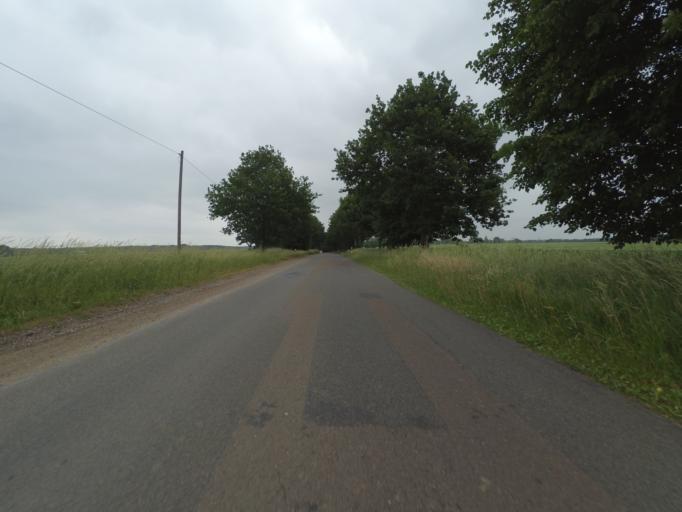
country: DE
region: Mecklenburg-Vorpommern
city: Spornitz
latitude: 53.3605
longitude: 11.7168
